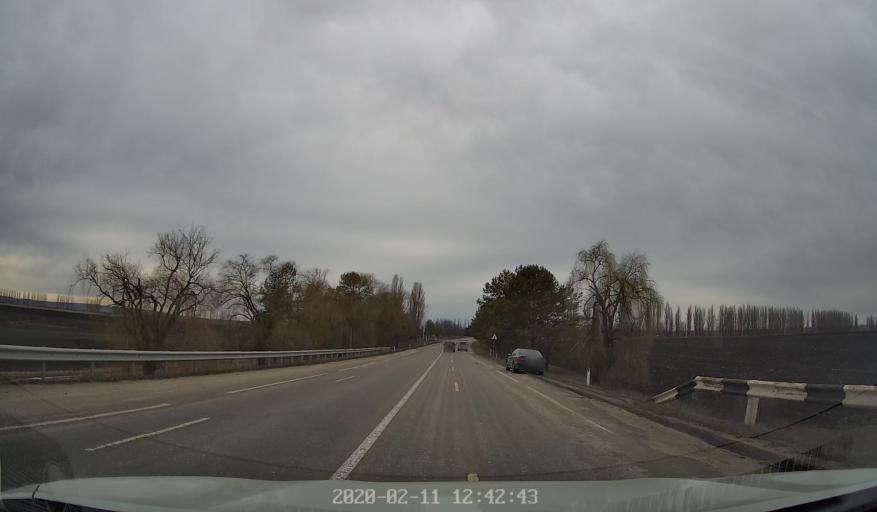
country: MD
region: Raionul Edinet
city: Edinet
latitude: 48.2254
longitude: 27.2183
